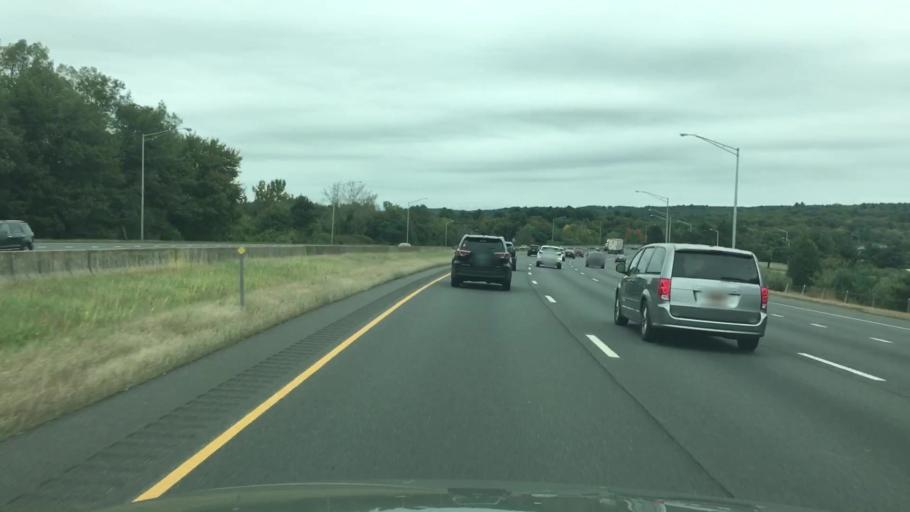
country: US
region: Connecticut
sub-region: Tolland County
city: Rockville
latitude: 41.8518
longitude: -72.4332
